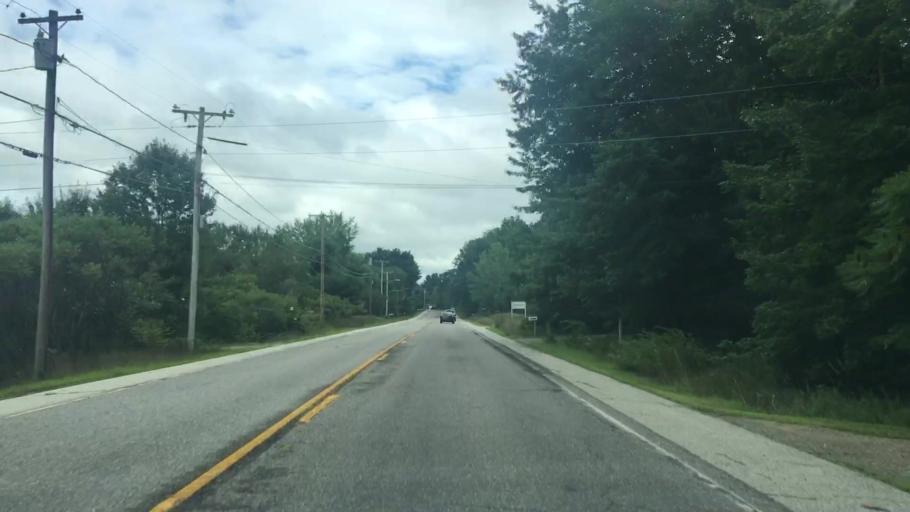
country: US
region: Maine
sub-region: York County
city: Lake Arrowhead
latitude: 43.6434
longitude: -70.7557
